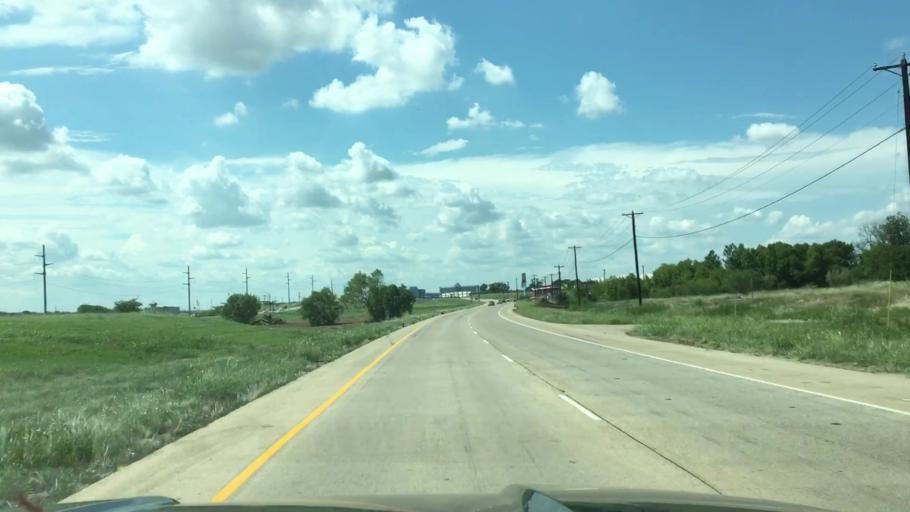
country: US
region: Texas
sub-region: Denton County
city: Roanoke
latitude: 33.0224
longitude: -97.2524
